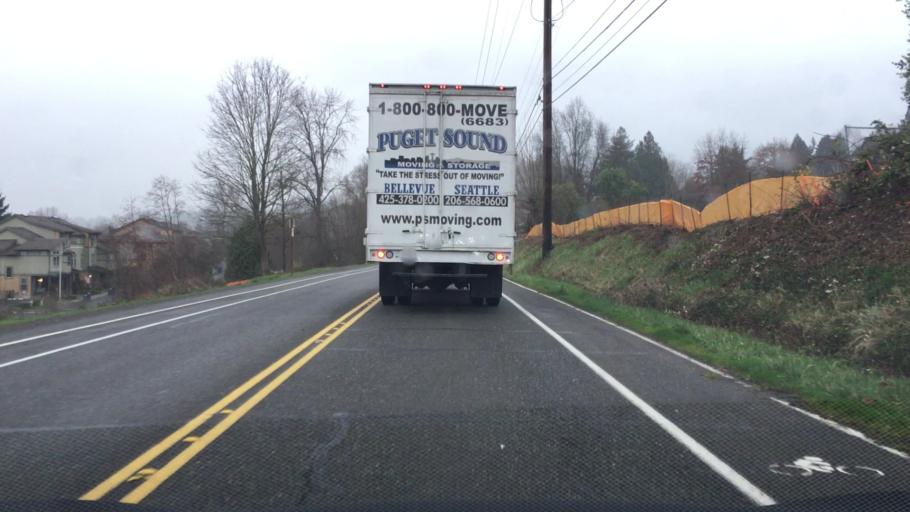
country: US
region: Washington
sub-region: King County
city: Renton
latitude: 47.5267
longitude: -122.2046
